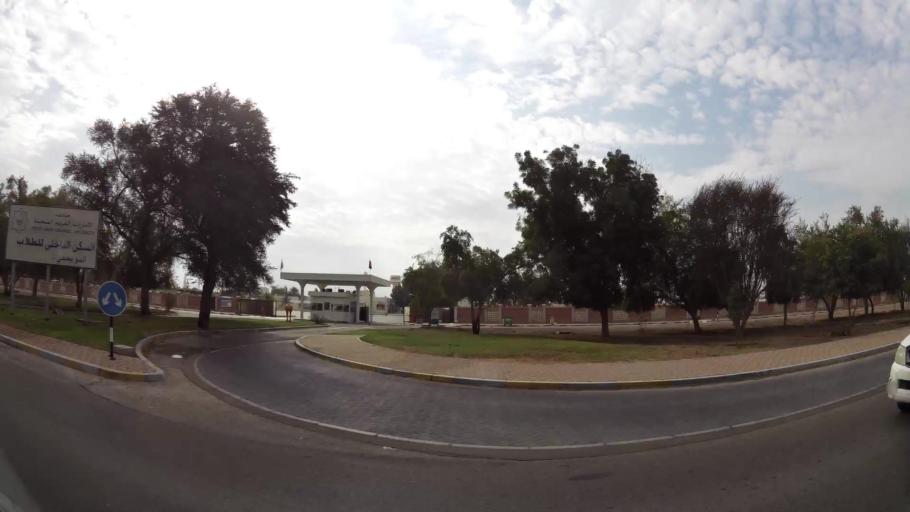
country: AE
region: Abu Dhabi
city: Al Ain
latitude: 24.2159
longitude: 55.7051
